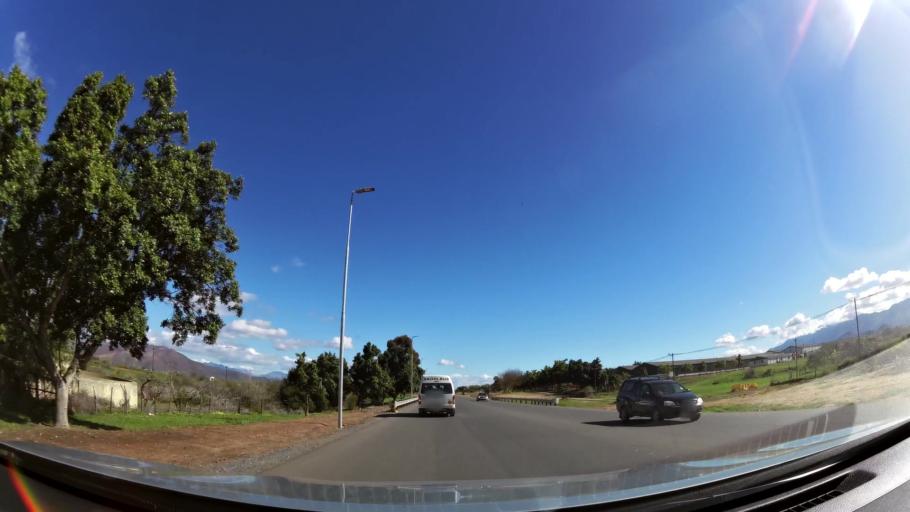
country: ZA
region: Western Cape
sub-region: Cape Winelands District Municipality
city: Ashton
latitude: -33.8368
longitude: 20.0386
